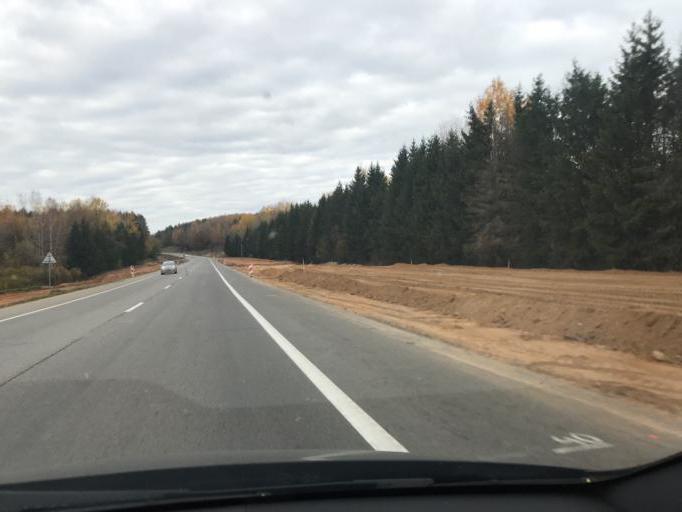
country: BY
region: Minsk
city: Slabada
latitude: 54.0351
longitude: 27.8448
